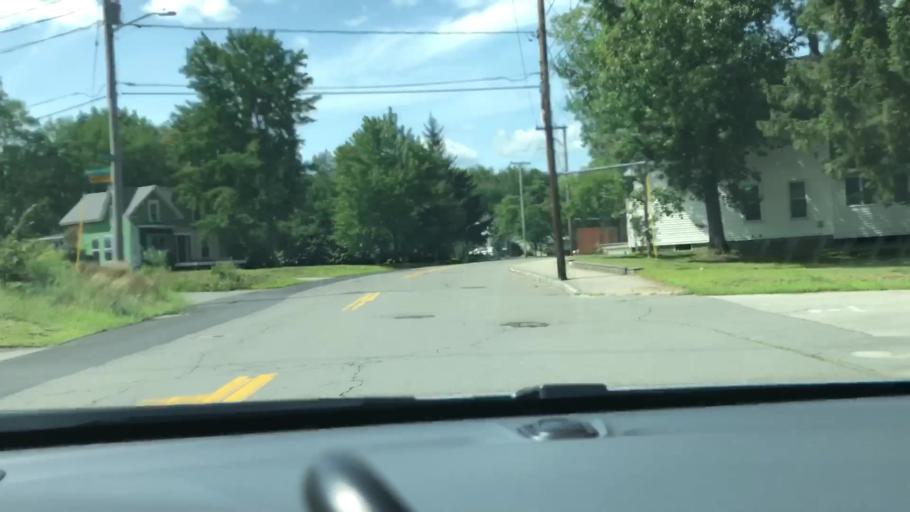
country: US
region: New Hampshire
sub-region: Hillsborough County
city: Pinardville
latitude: 42.9807
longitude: -71.4923
